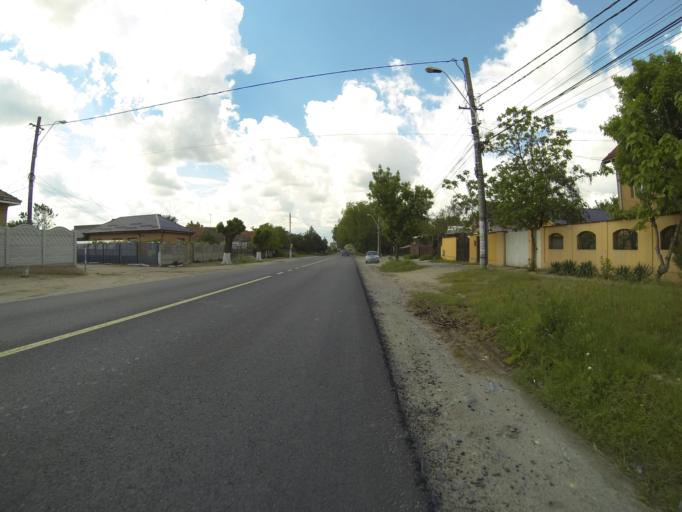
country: RO
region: Dolj
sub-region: Municipiul Craiova
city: Facai
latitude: 44.2739
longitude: 23.8162
